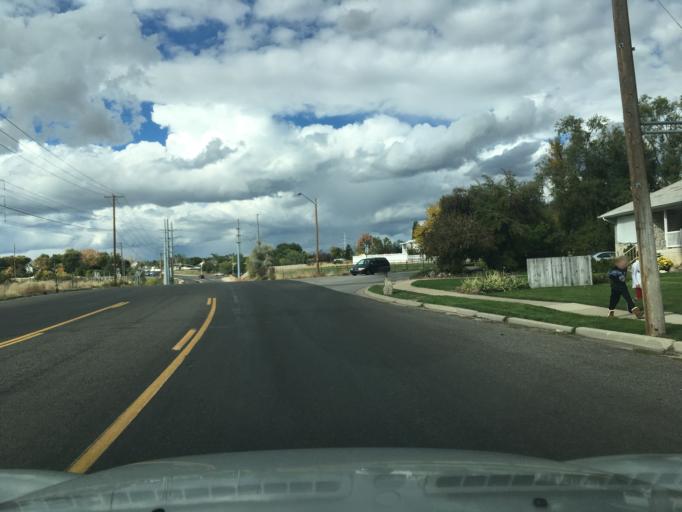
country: US
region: Utah
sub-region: Davis County
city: Layton
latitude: 41.0717
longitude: -111.9574
